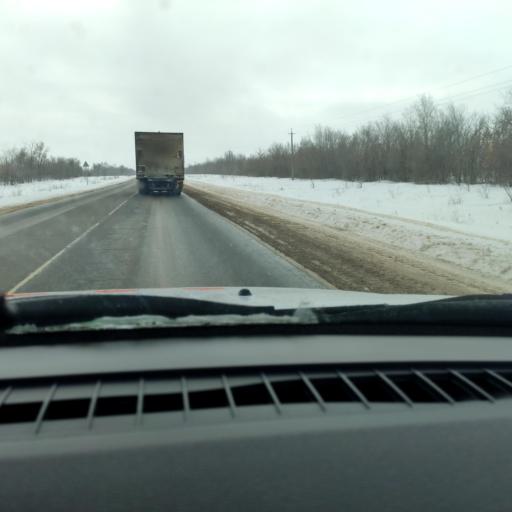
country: RU
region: Samara
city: Dubovyy Umet
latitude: 52.7802
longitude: 50.4935
